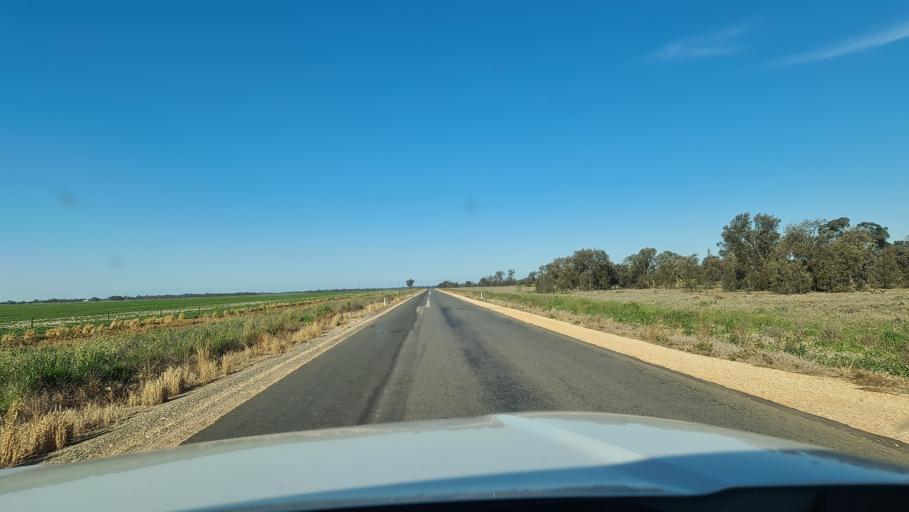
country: AU
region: Victoria
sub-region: Horsham
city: Horsham
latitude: -36.4492
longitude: 142.5512
